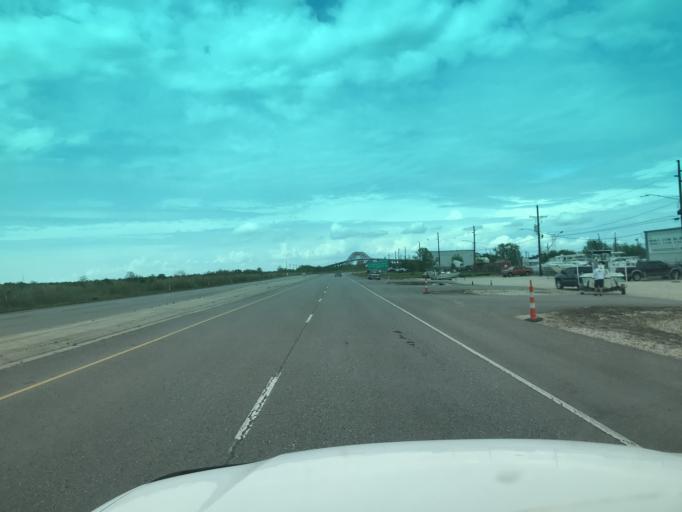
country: US
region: Louisiana
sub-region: Saint Bernard Parish
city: Chalmette
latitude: 29.9860
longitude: -89.9440
